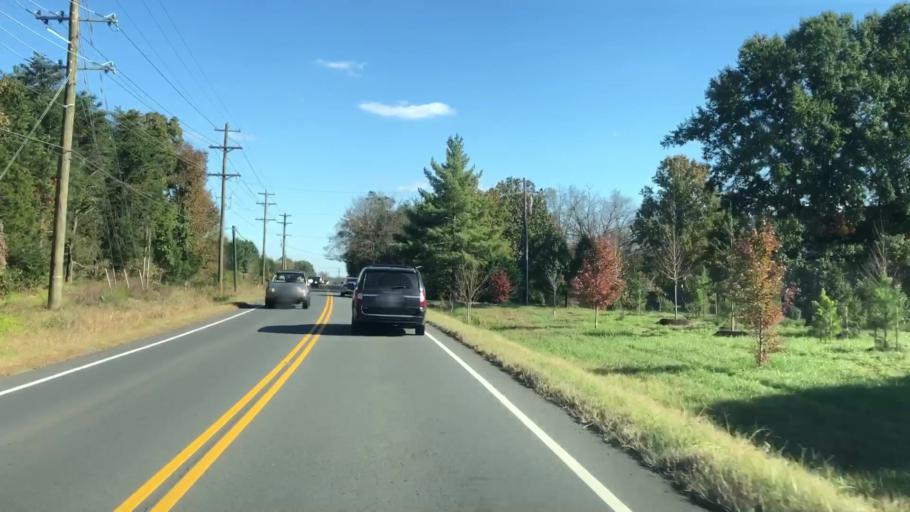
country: US
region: Virginia
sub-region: Prince William County
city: Linton Hall
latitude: 38.7342
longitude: -77.5889
